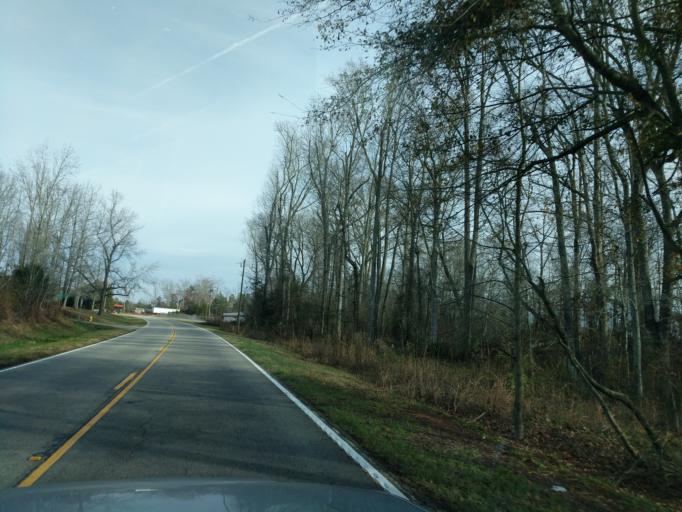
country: US
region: South Carolina
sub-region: Pickens County
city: Liberty
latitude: 34.7051
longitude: -82.6292
